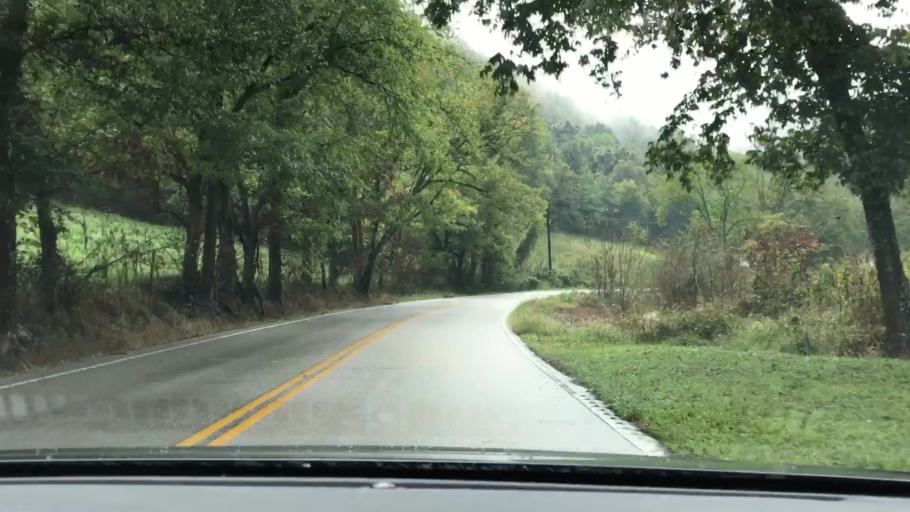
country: US
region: Tennessee
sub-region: Macon County
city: Lafayette
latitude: 36.4088
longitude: -85.9310
